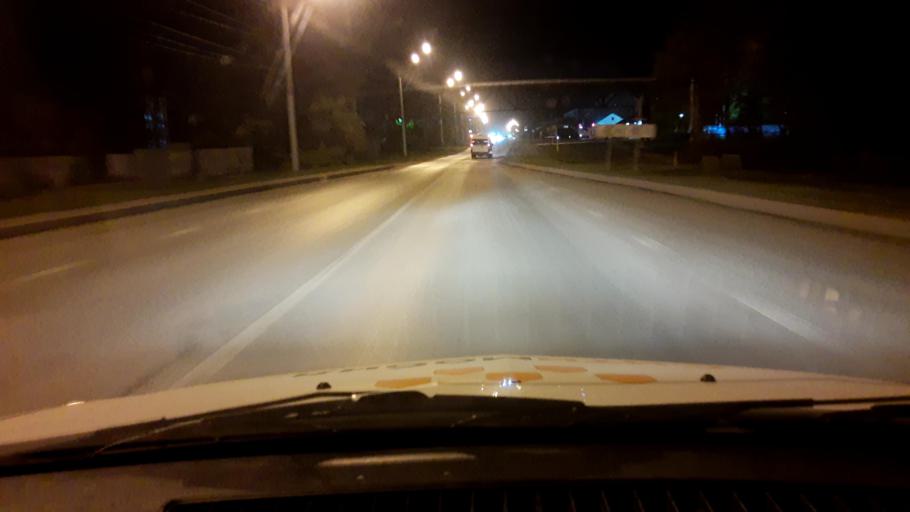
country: RU
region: Bashkortostan
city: Iglino
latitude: 54.7639
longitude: 56.2392
